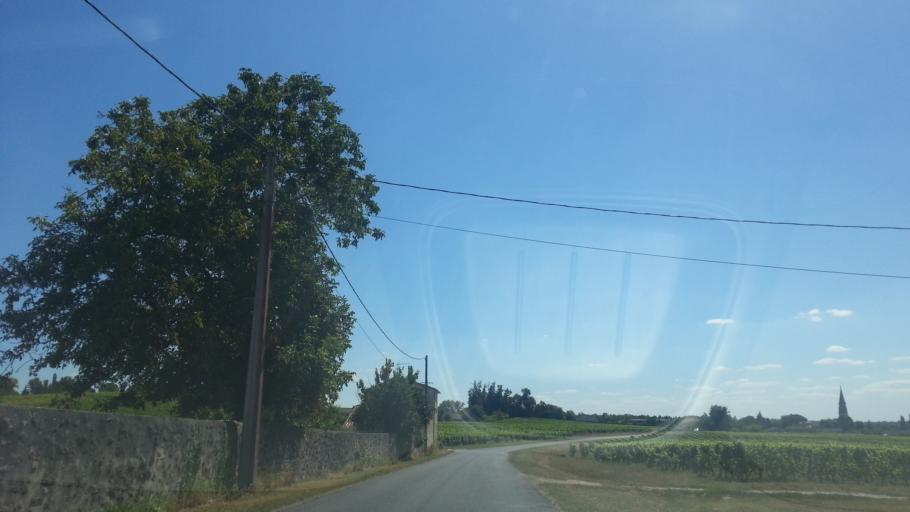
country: FR
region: Aquitaine
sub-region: Departement de la Gironde
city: Illats
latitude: 44.5500
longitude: -0.3521
